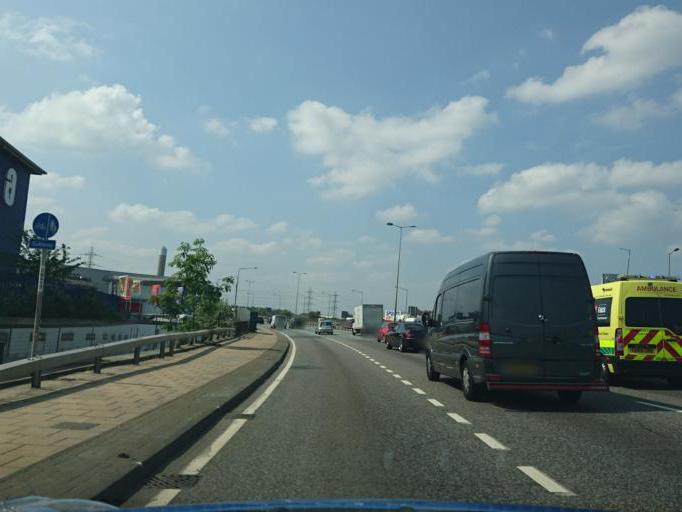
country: GB
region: England
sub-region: Greater London
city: Walthamstow
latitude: 51.6112
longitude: -0.0315
